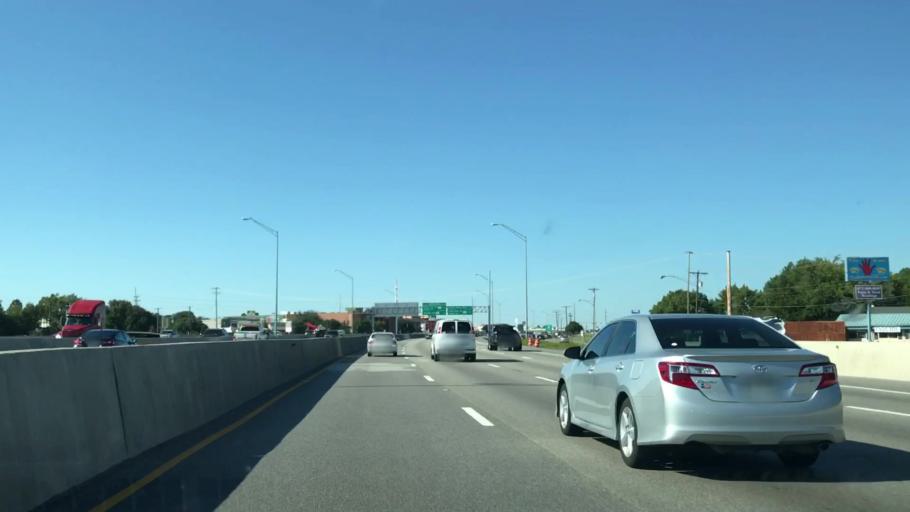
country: US
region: Texas
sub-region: Denton County
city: Lewisville
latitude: 33.0408
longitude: -97.0047
